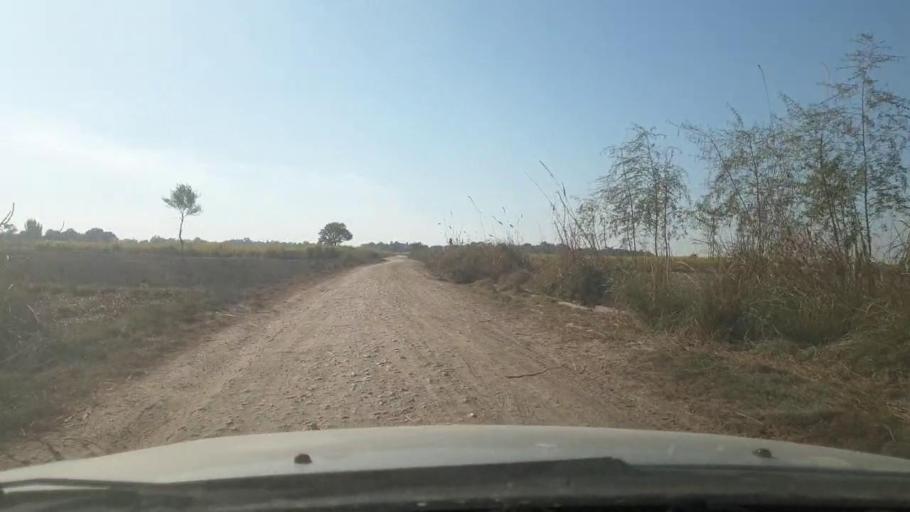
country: PK
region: Sindh
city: Ghotki
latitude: 27.9781
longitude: 69.1946
